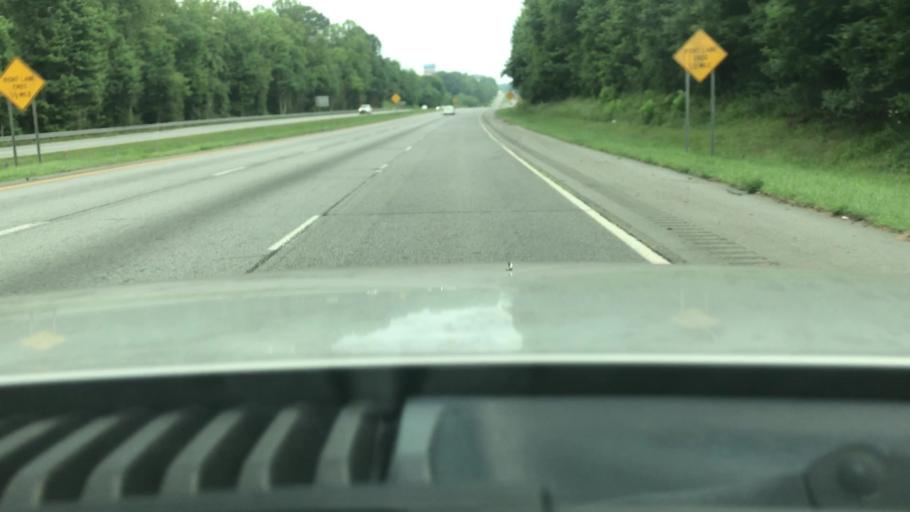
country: US
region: North Carolina
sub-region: Yadkin County
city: Jonesville
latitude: 36.2574
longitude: -80.8231
